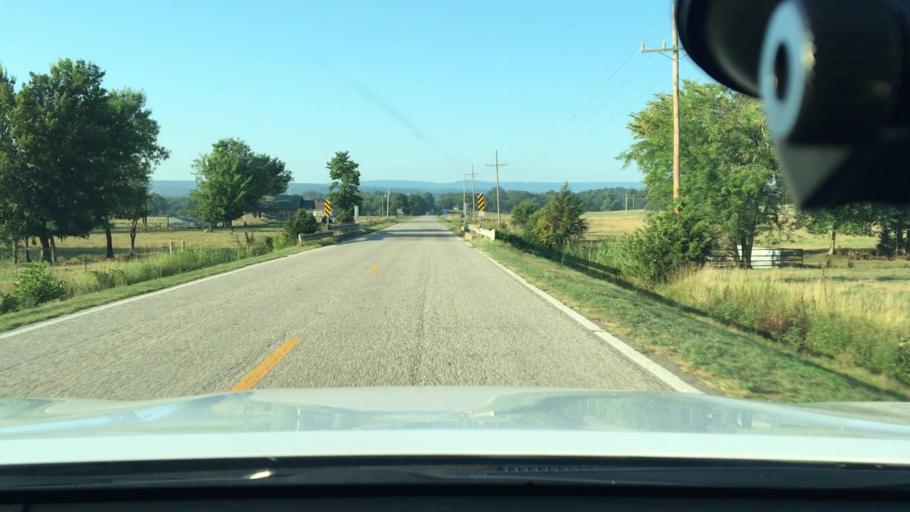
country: US
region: Arkansas
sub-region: Logan County
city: Paris
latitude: 35.3255
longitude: -93.6321
